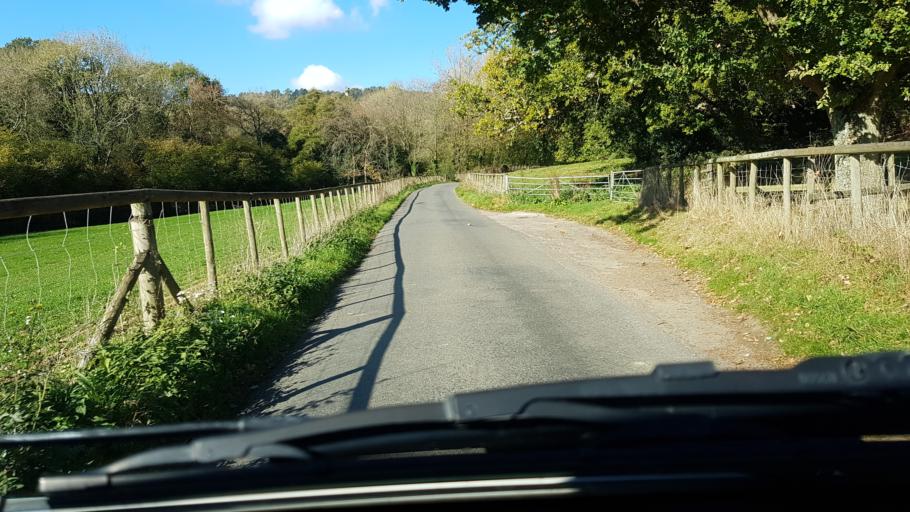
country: GB
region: England
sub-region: Surrey
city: Ockley
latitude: 51.1681
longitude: -0.3595
